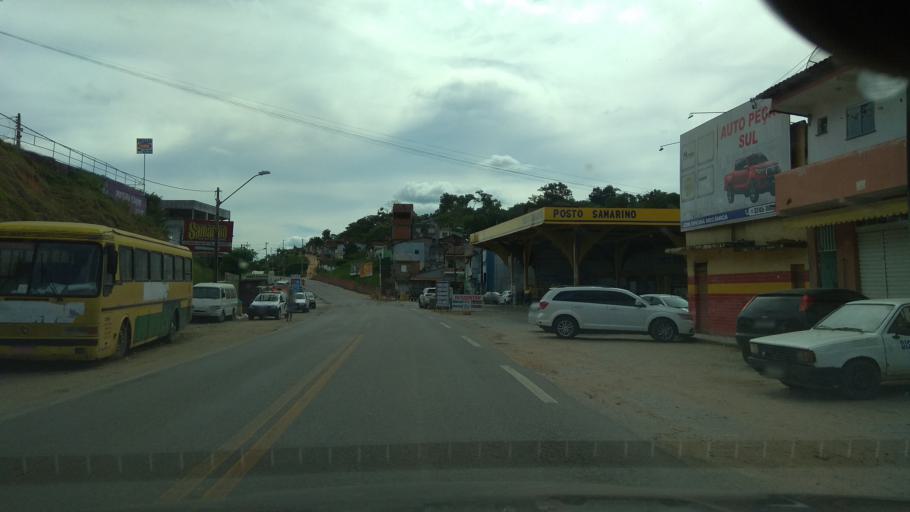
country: BR
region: Bahia
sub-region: Ubata
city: Ubata
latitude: -14.2125
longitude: -39.5179
